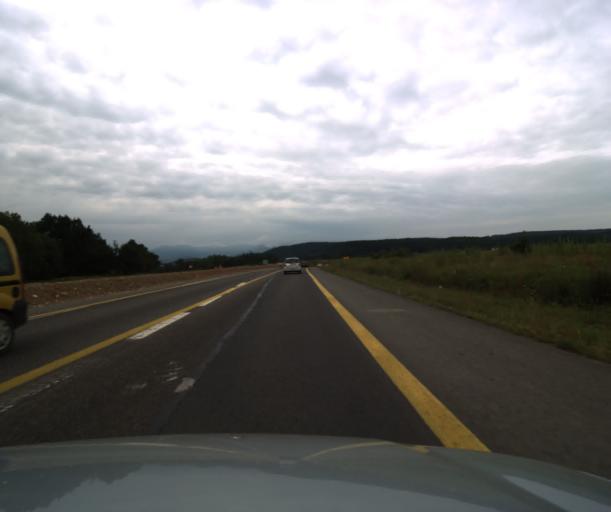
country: FR
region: Midi-Pyrenees
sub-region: Departement des Hautes-Pyrenees
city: Ossun
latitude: 43.1648
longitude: -0.0101
